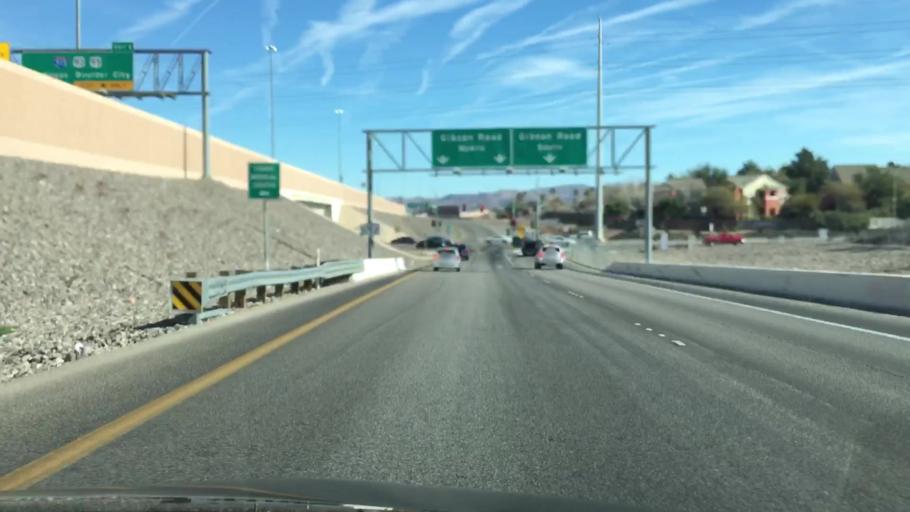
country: US
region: Nevada
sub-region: Clark County
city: Henderson
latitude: 36.0313
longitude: -115.0311
